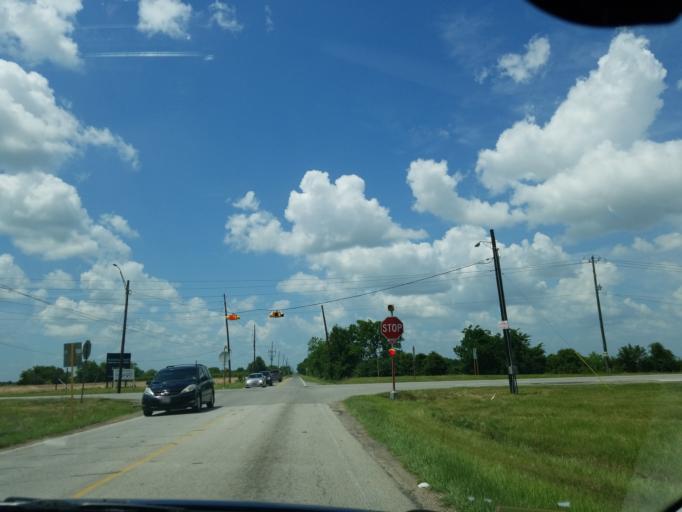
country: US
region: Texas
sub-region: Harris County
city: Katy
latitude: 29.8746
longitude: -95.8072
